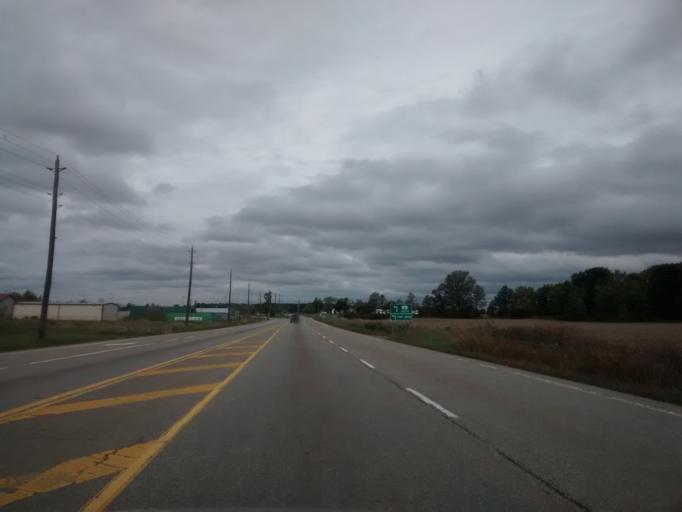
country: CA
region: Ontario
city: Ancaster
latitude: 43.0915
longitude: -79.9527
